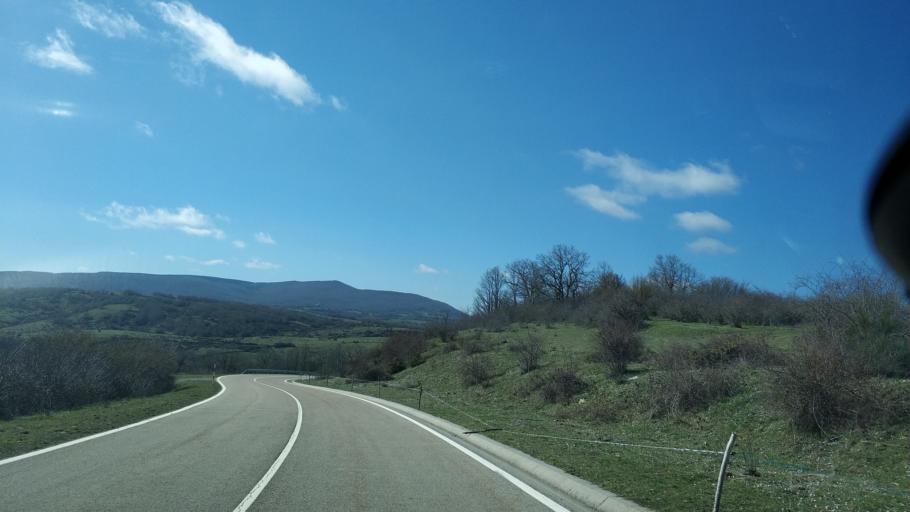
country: ES
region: Cantabria
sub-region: Provincia de Cantabria
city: Mataporquera
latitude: 42.9071
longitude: -4.0814
